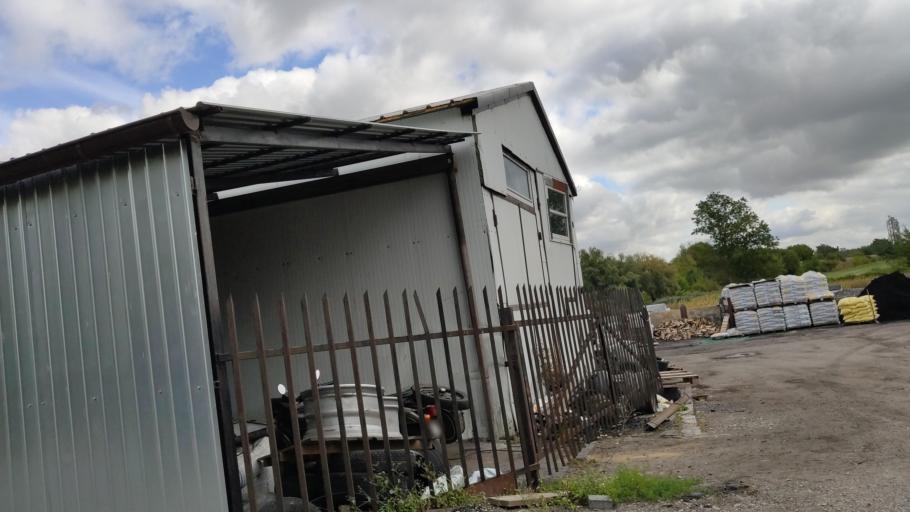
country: PL
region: Kujawsko-Pomorskie
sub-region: Powiat zninski
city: Barcin
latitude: 52.8450
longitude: 17.9543
